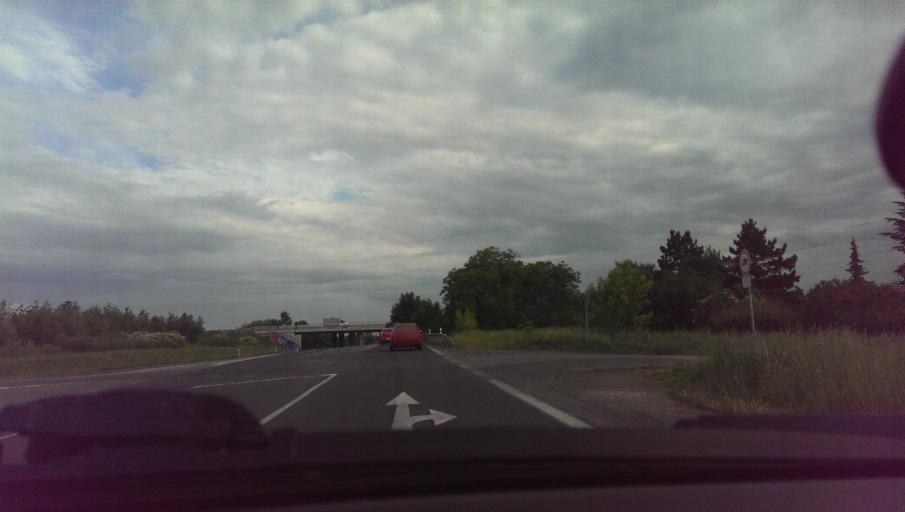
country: CZ
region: Zlin
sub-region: Okres Kromeriz
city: Kromeriz
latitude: 49.3098
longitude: 17.3781
